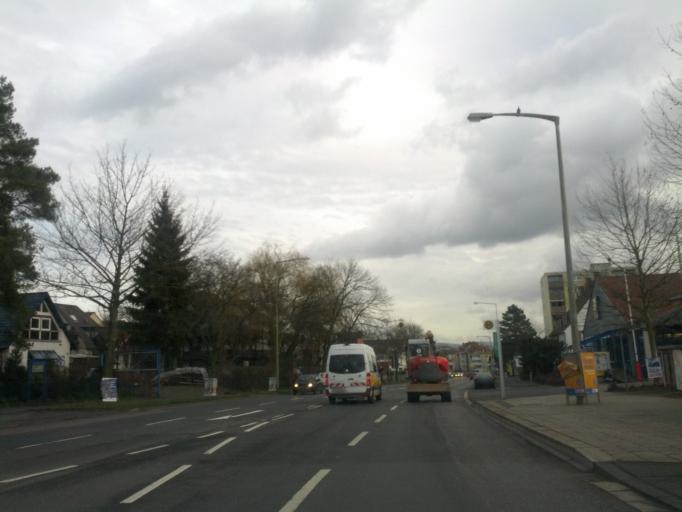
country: DE
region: Hesse
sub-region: Regierungsbezirk Kassel
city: Kassel
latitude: 51.3091
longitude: 9.4577
